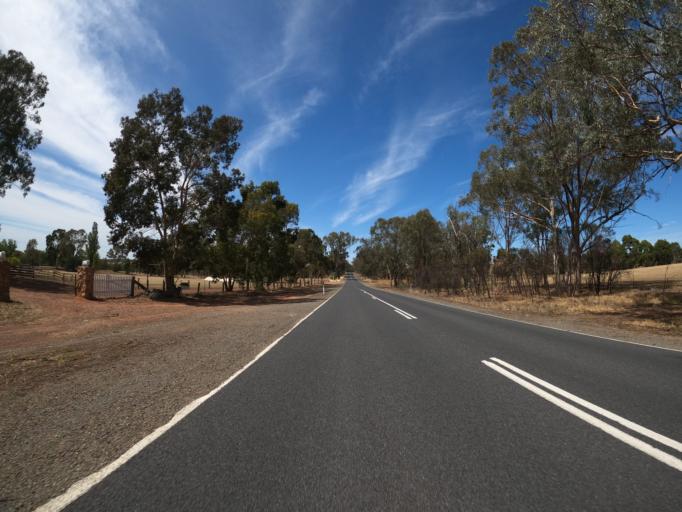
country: AU
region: Victoria
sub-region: Benalla
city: Benalla
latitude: -36.3850
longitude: 145.9789
